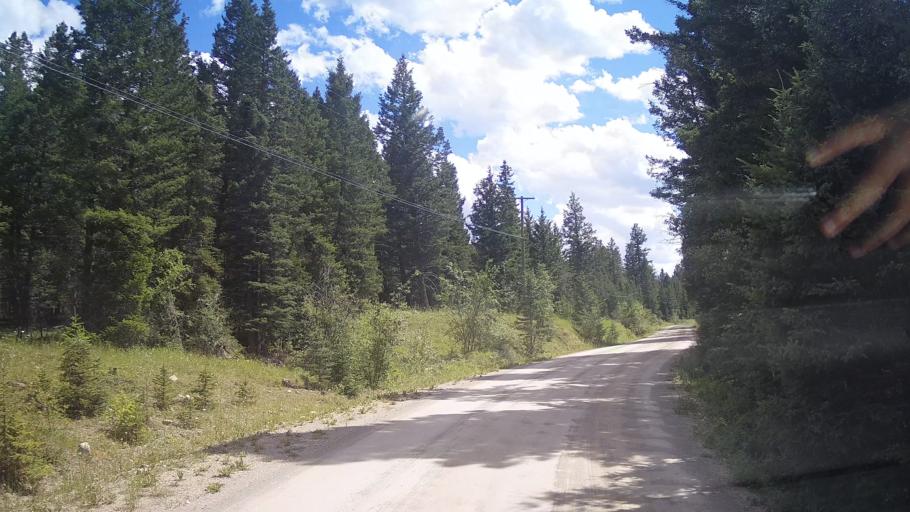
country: CA
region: British Columbia
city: Lillooet
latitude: 51.2859
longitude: -121.9683
